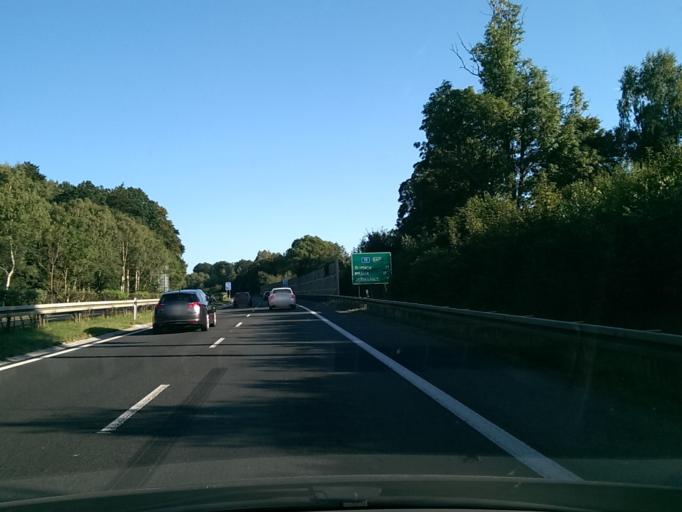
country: CZ
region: Liberecky
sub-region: Okres Liberec
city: Liberec
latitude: 50.7265
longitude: 15.0591
